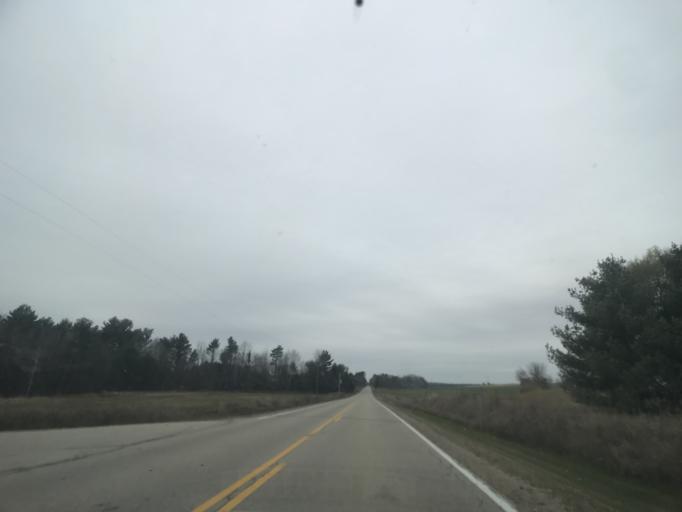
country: US
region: Wisconsin
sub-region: Oconto County
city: Gillett
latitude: 44.9836
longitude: -88.3131
